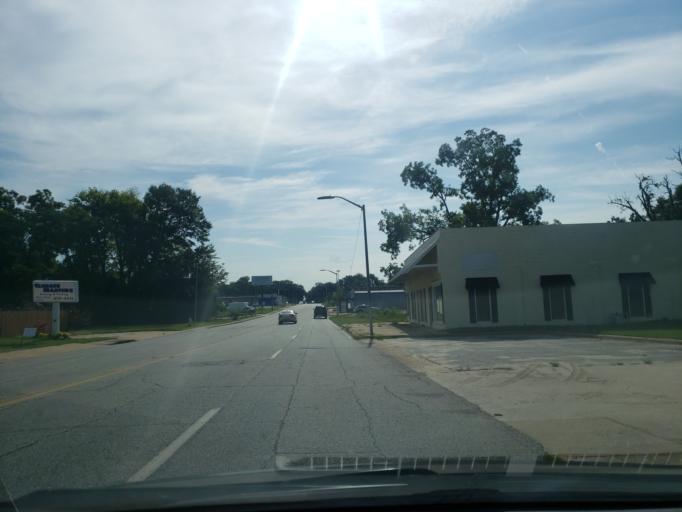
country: US
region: Georgia
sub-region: Dougherty County
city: Albany
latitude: 31.5785
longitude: -84.1684
